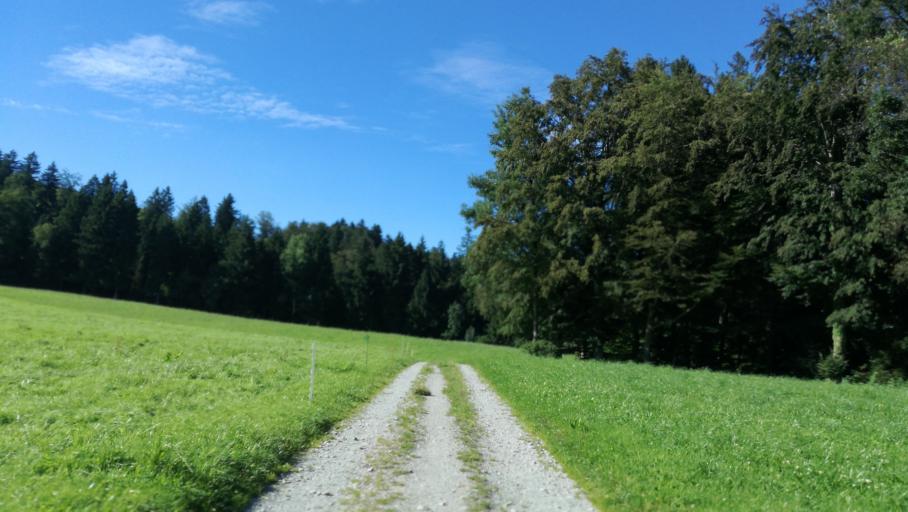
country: CH
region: Zug
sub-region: Zug
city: Unterageri
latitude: 47.1528
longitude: 8.5537
